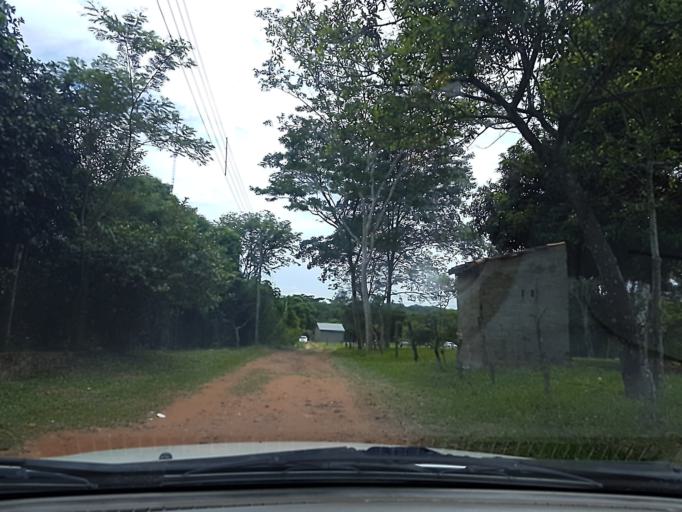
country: PY
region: Central
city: Limpio
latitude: -25.2369
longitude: -57.4458
